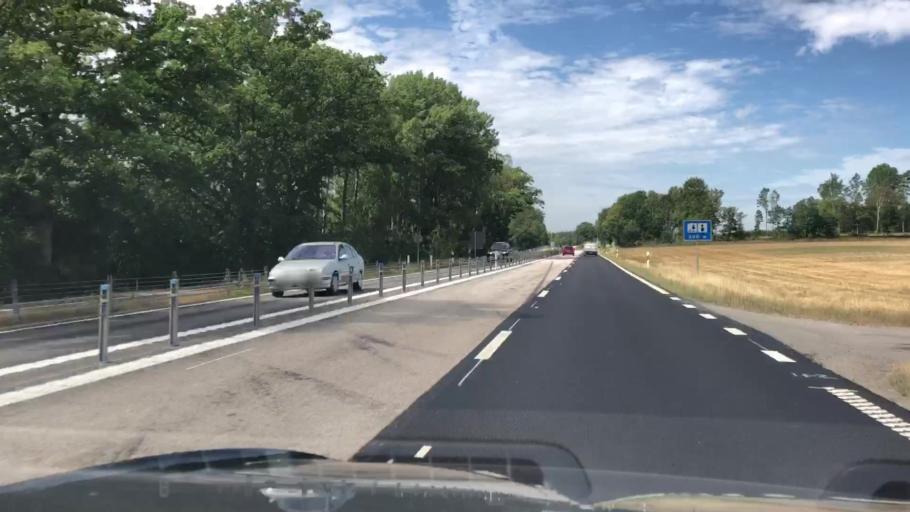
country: SE
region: Blekinge
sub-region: Karlskrona Kommun
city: Nattraby
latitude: 56.1976
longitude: 15.4312
